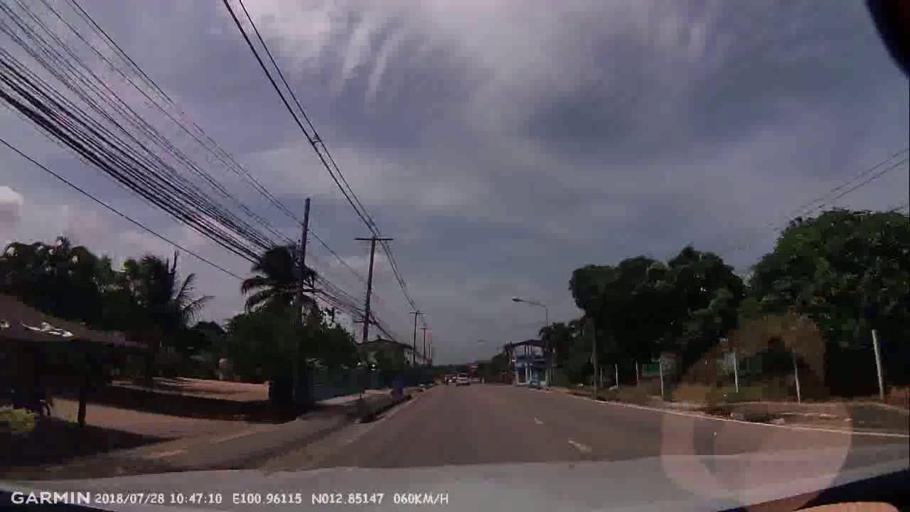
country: TH
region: Chon Buri
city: Phatthaya
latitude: 12.8513
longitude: 100.9611
